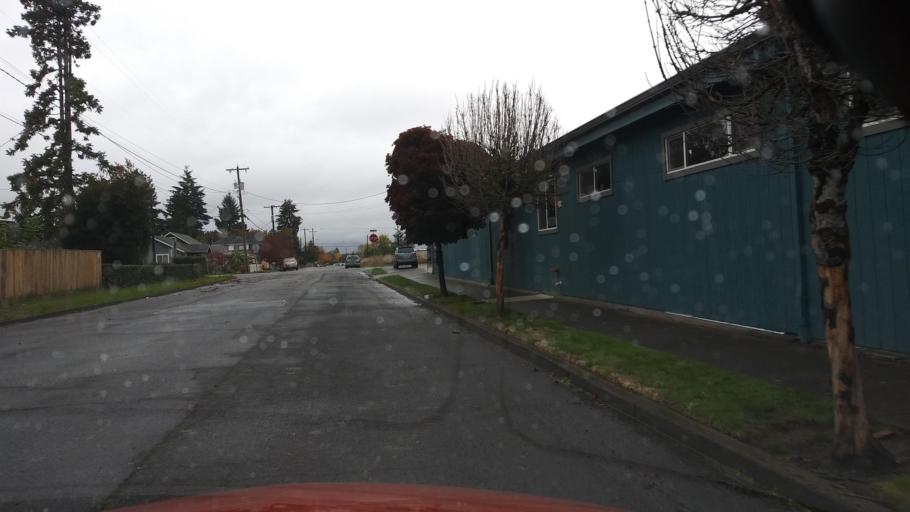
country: US
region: Oregon
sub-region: Washington County
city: Cornelius
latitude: 45.5193
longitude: -123.0560
